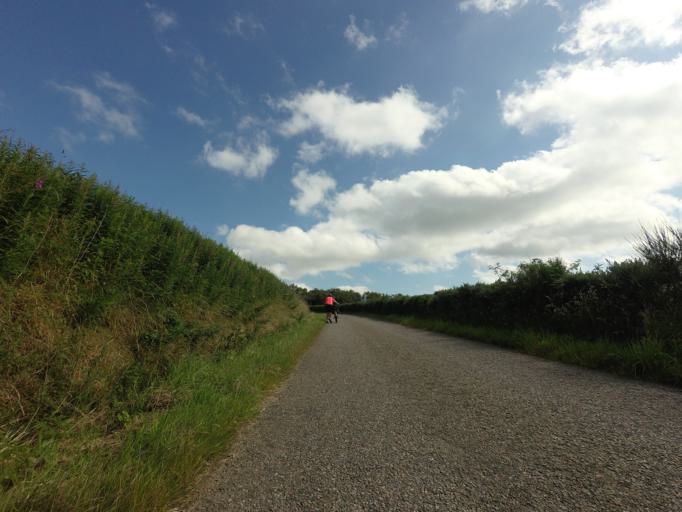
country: GB
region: Scotland
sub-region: Aberdeenshire
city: Banff
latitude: 57.5943
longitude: -2.5097
